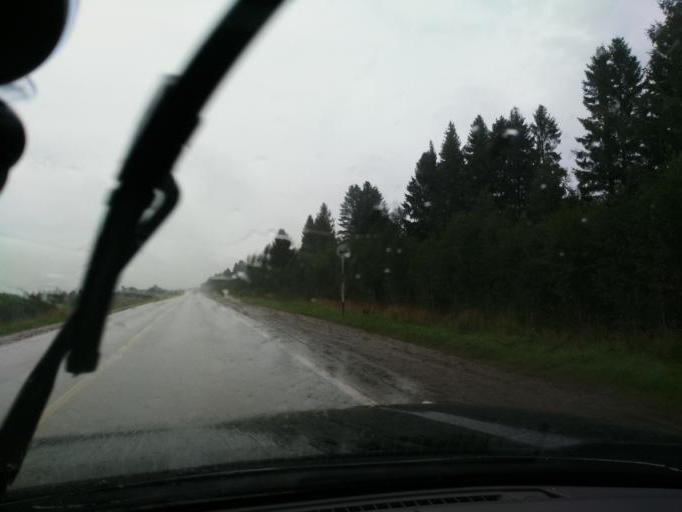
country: RU
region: Perm
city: Osa
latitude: 57.3368
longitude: 55.5852
